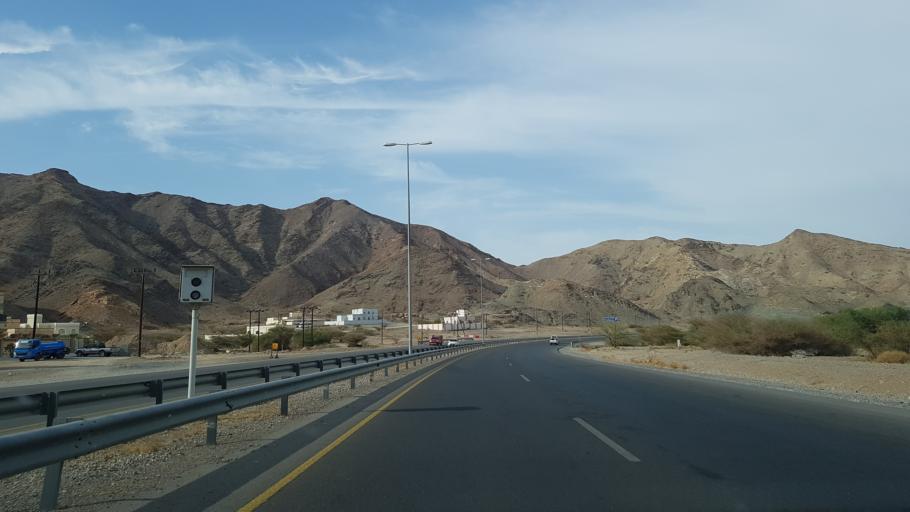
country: OM
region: Muhafazat ad Dakhiliyah
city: Bidbid
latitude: 23.4087
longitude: 58.0806
